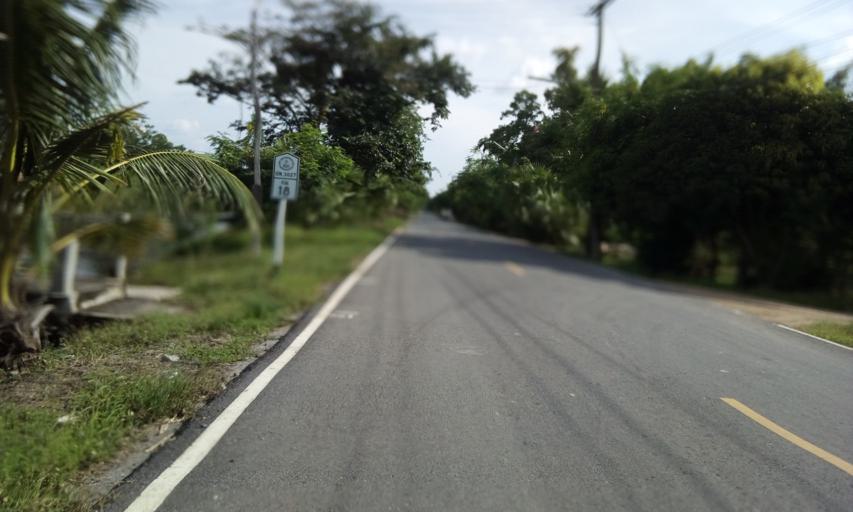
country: TH
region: Pathum Thani
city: Nong Suea
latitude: 14.2155
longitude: 100.8229
